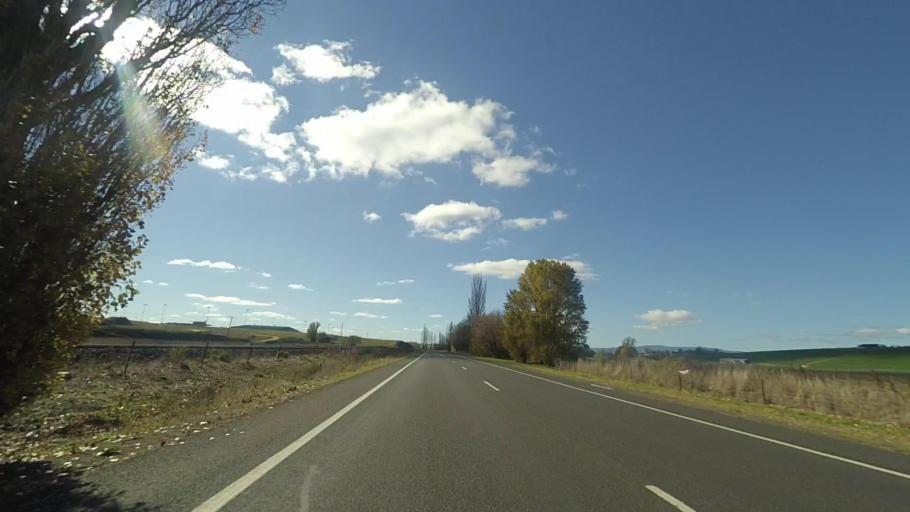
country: AU
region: New South Wales
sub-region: Bathurst Regional
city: Bathurst
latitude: -33.4565
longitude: 149.5750
